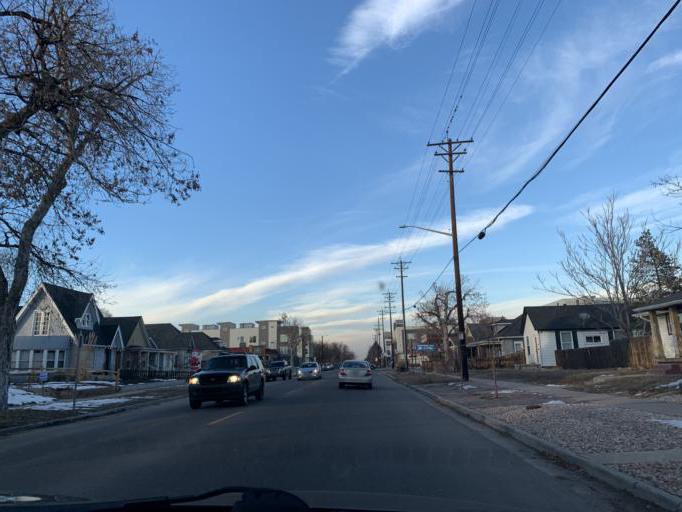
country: US
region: Colorado
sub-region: Adams County
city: Berkley
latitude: 39.7847
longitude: -105.0345
